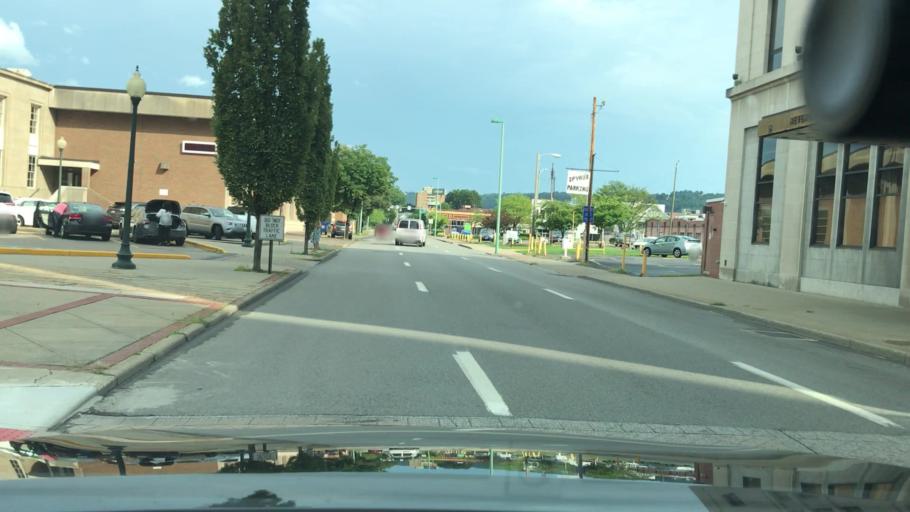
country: US
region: West Virginia
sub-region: Kanawha County
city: Charleston
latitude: 38.3498
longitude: -81.6324
